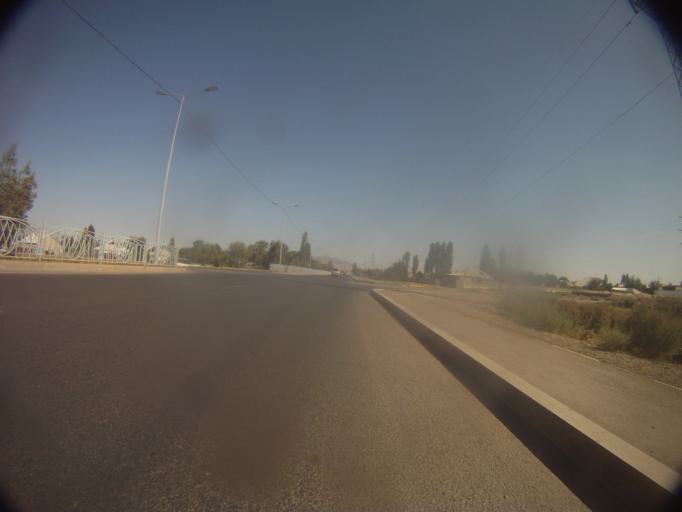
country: KZ
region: Zhambyl
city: Taraz
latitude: 42.9214
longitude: 71.4041
